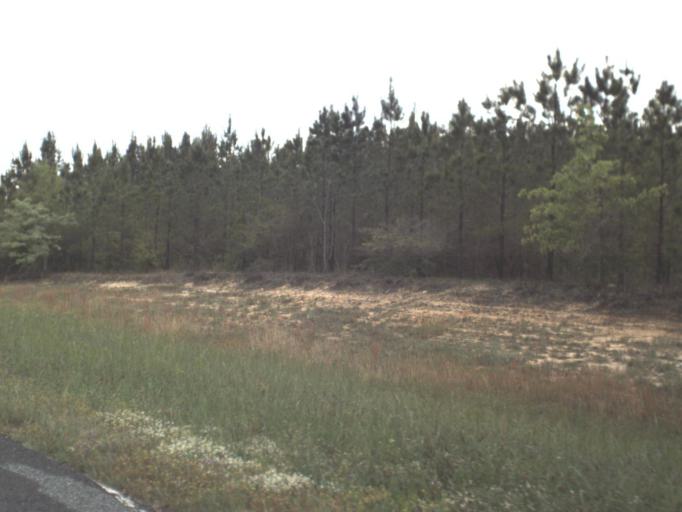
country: US
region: Florida
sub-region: Escambia County
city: Molino
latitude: 30.8060
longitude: -87.3363
